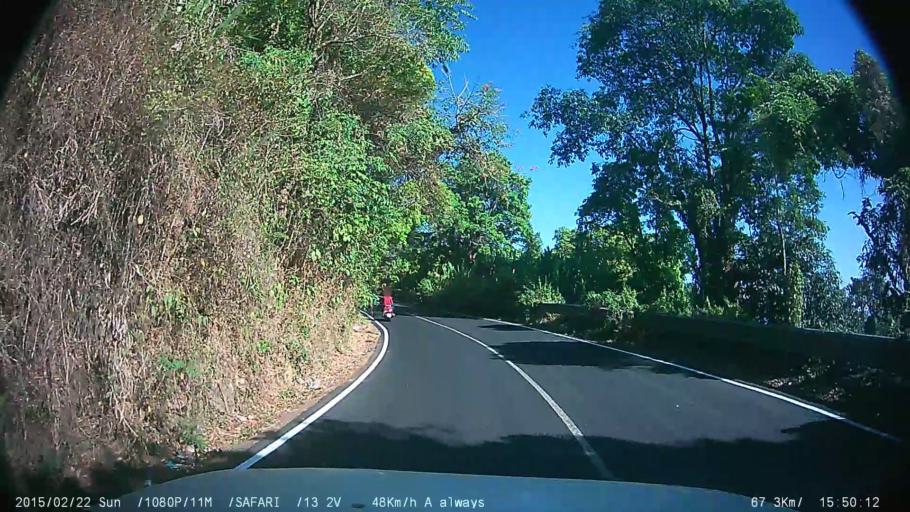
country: IN
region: Kerala
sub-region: Kottayam
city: Erattupetta
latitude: 9.5705
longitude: 77.0014
